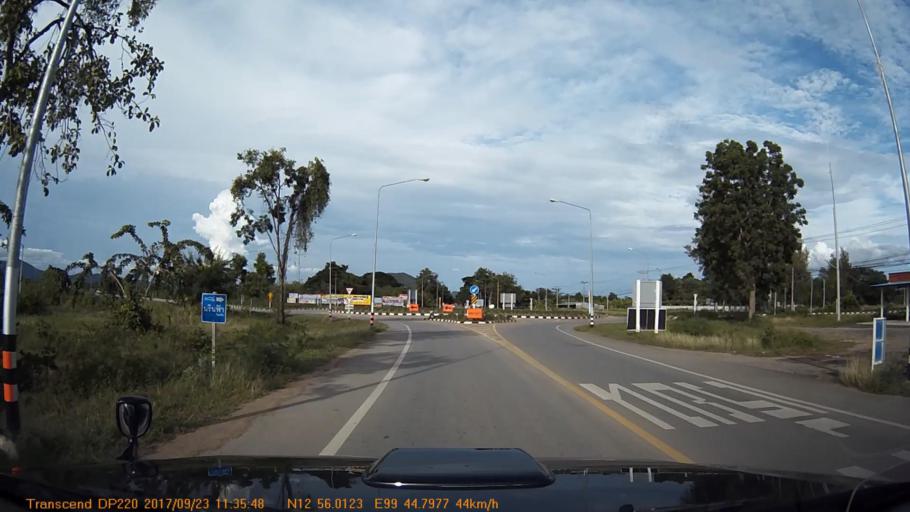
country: TH
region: Phetchaburi
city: Kaeng Krachan
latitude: 12.9334
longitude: 99.7465
